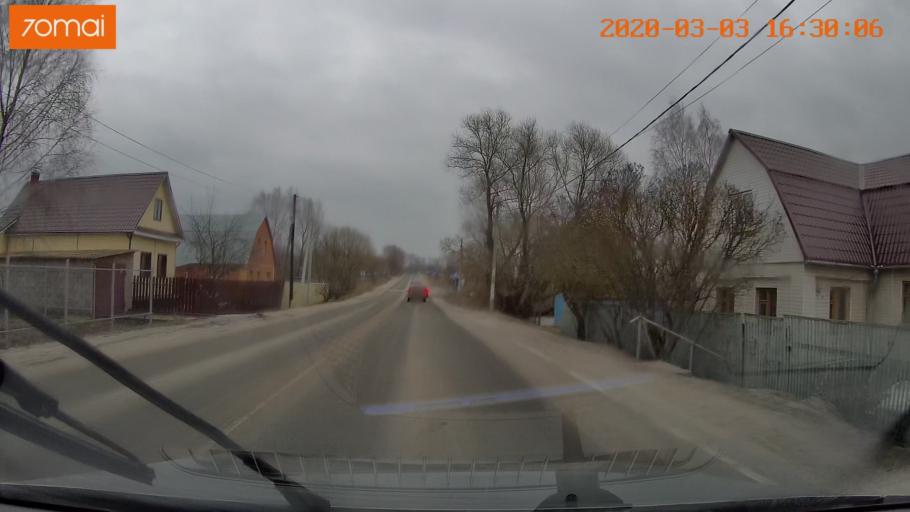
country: RU
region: Moskovskaya
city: Konobeyevo
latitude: 55.4344
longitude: 38.7085
